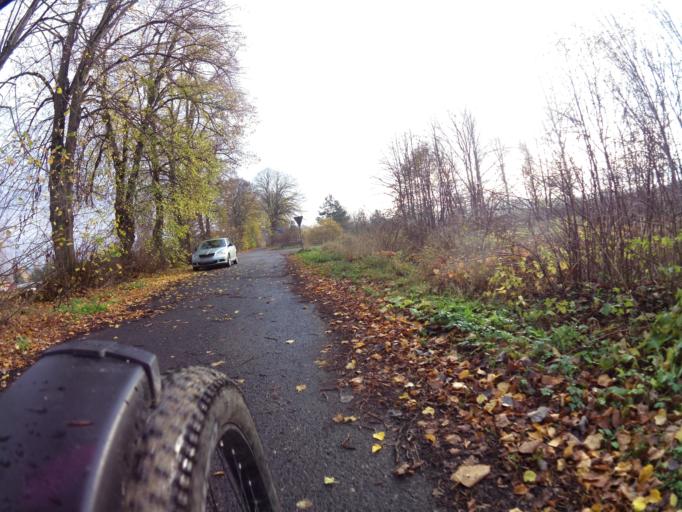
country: PL
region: Pomeranian Voivodeship
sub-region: Powiat wejherowski
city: Gniewino
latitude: 54.7135
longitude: 18.0943
